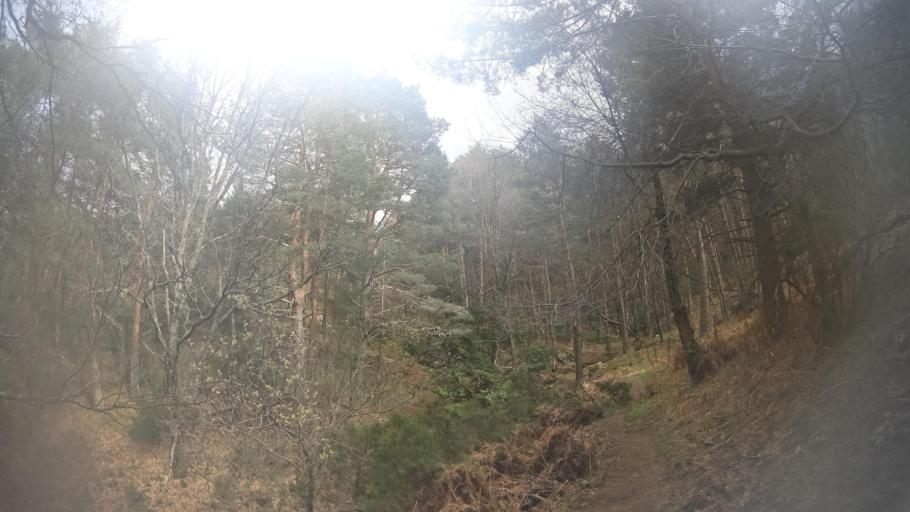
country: ES
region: Madrid
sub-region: Provincia de Madrid
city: Canencia
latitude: 40.8741
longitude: -3.7686
